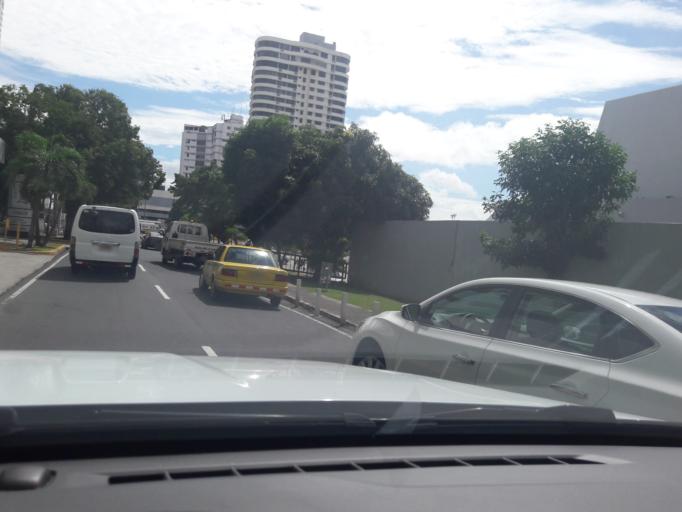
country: PA
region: Panama
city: Panama
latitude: 8.9906
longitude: -79.5000
